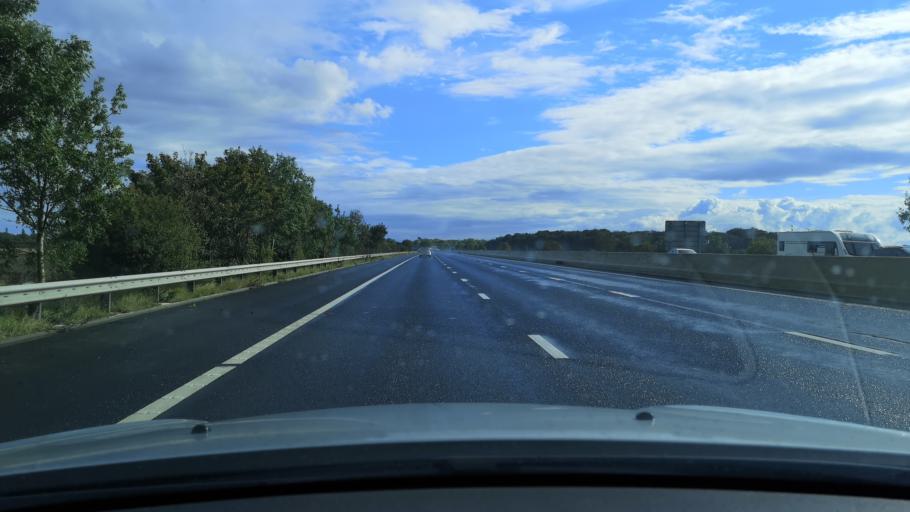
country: GB
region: England
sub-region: Doncaster
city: Norton
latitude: 53.6948
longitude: -1.1735
